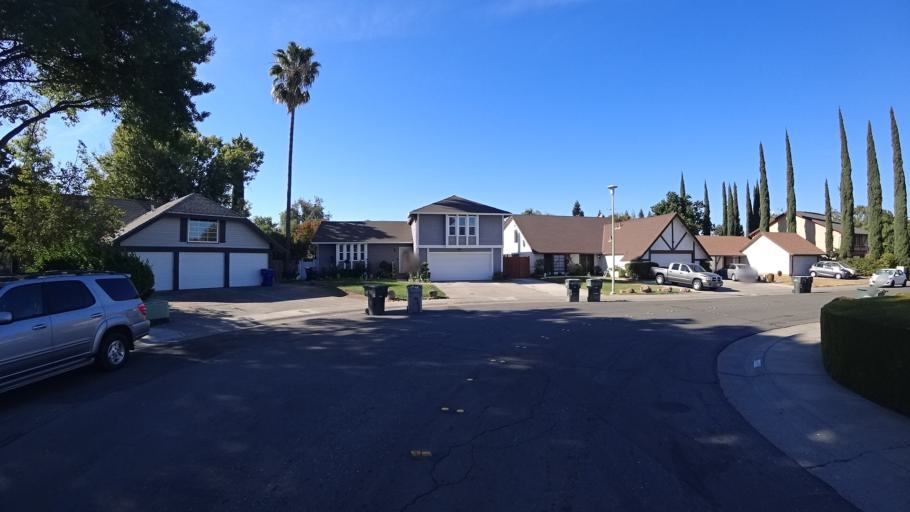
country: US
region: California
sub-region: Sacramento County
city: Florin
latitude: 38.4606
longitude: -121.4256
